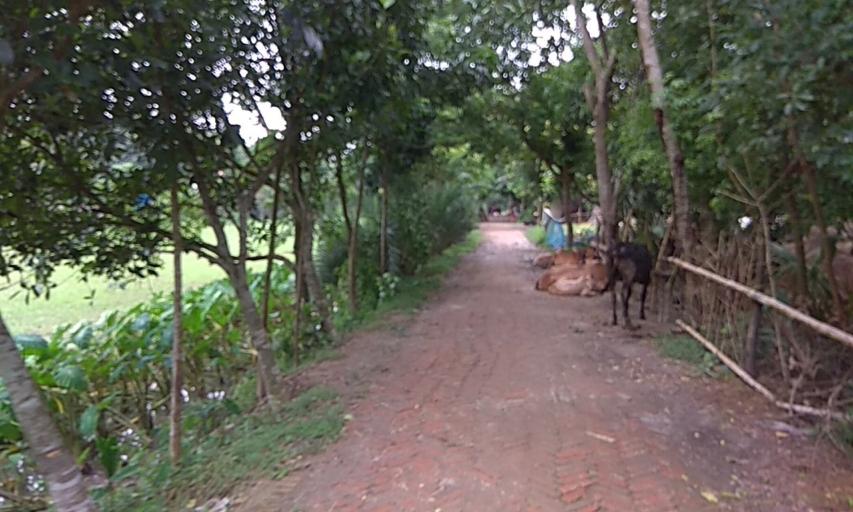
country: BD
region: Dhaka
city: Dohar
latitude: 23.5415
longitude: 89.9919
